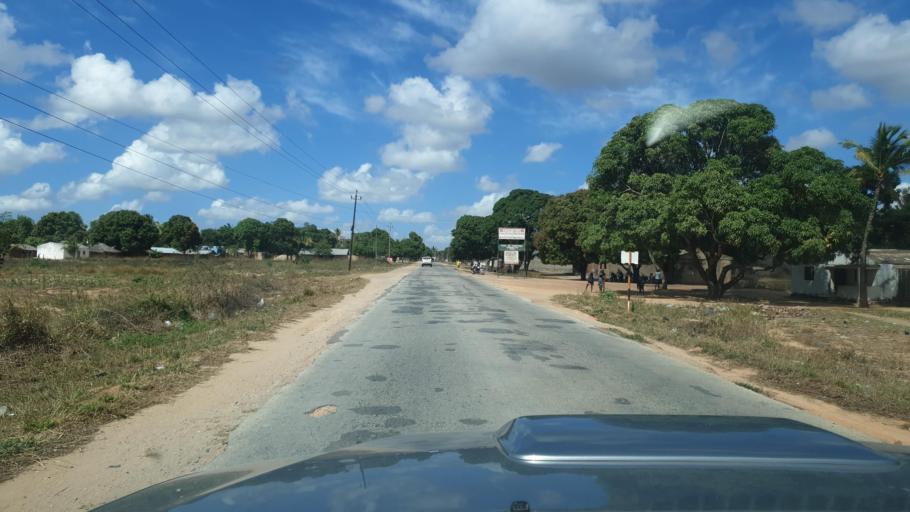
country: MZ
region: Nampula
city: Nacala
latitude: -14.5049
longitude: 40.6976
